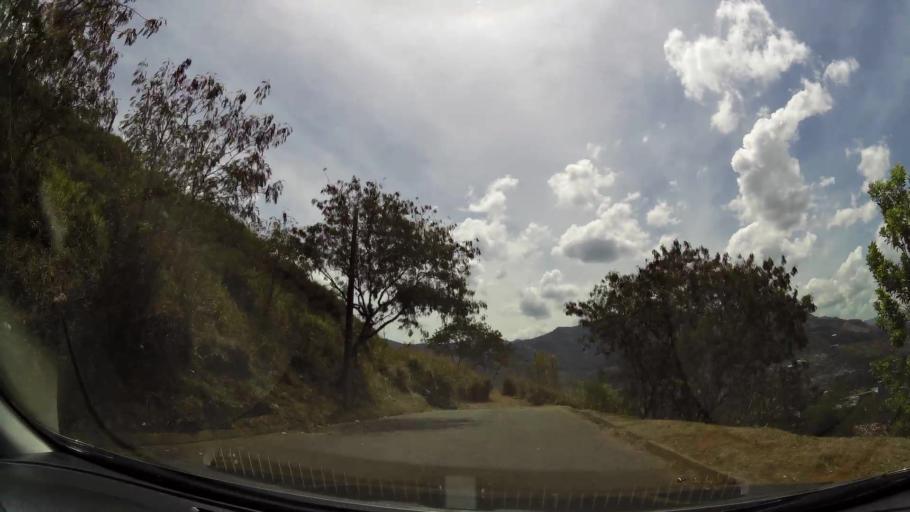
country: CO
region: Antioquia
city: Bello
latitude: 6.3485
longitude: -75.5446
